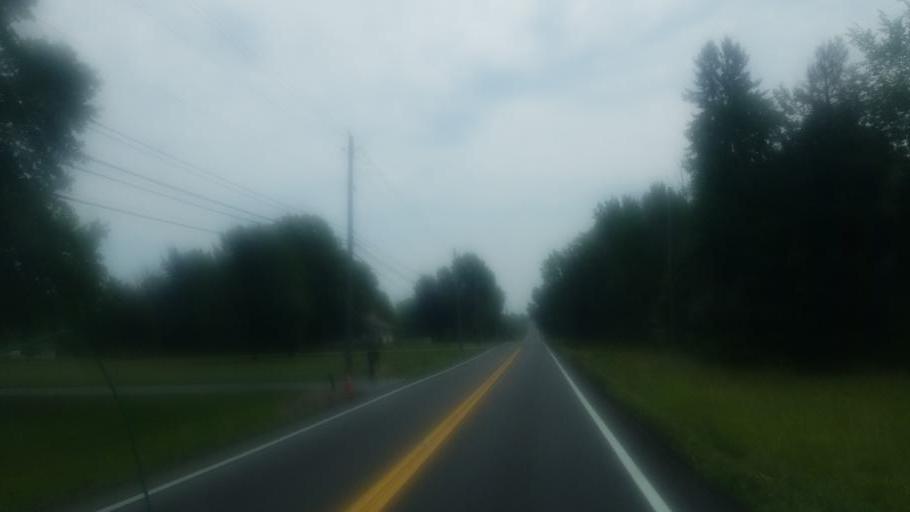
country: US
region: Ohio
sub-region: Columbiana County
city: Columbiana
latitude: 40.9442
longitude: -80.7301
